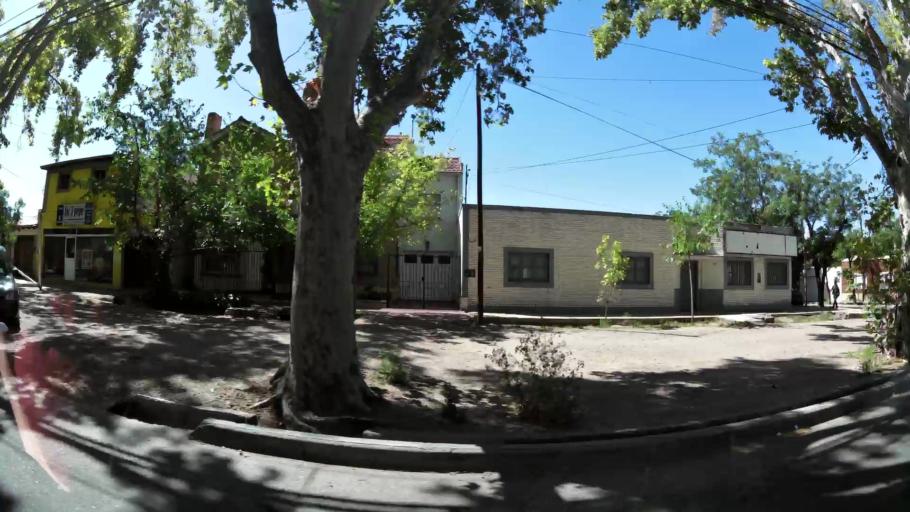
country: AR
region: Mendoza
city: Mendoza
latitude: -32.8961
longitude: -68.8107
